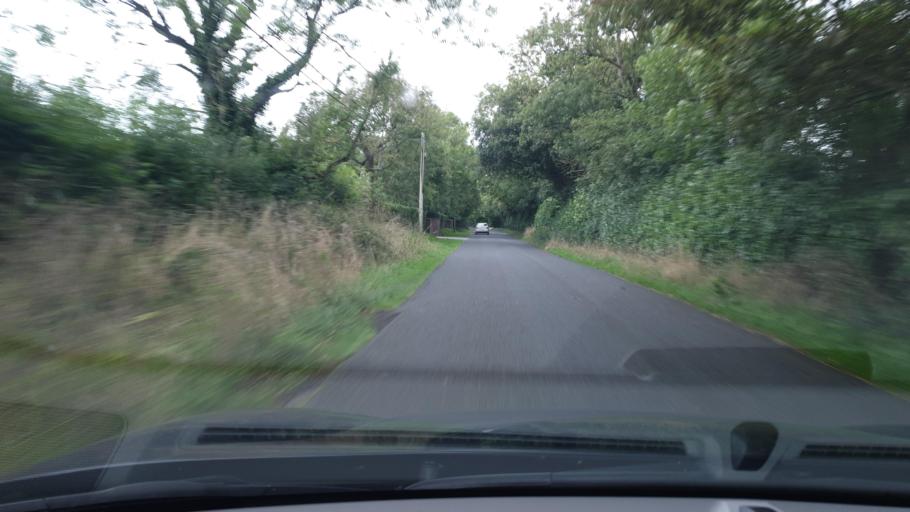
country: IE
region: Leinster
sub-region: An Mhi
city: Dunshaughlin
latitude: 53.5506
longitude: -6.5328
